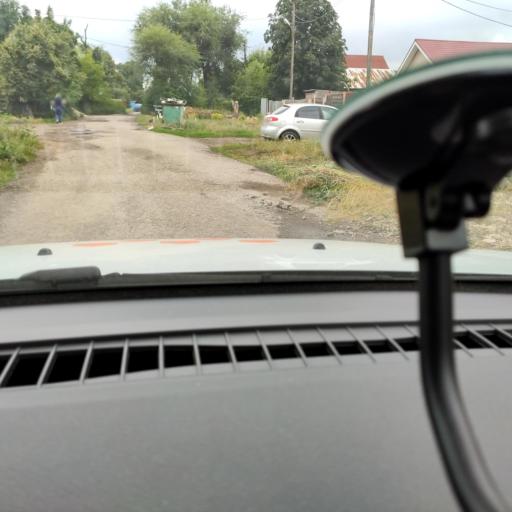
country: RU
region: Samara
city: Petra-Dubrava
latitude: 53.2493
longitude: 50.3331
